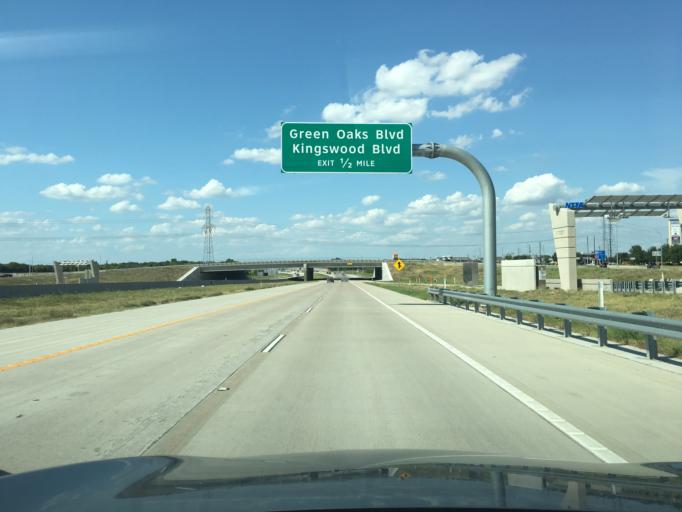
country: US
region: Texas
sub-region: Tarrant County
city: Arlington
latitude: 32.6459
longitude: -97.0623
